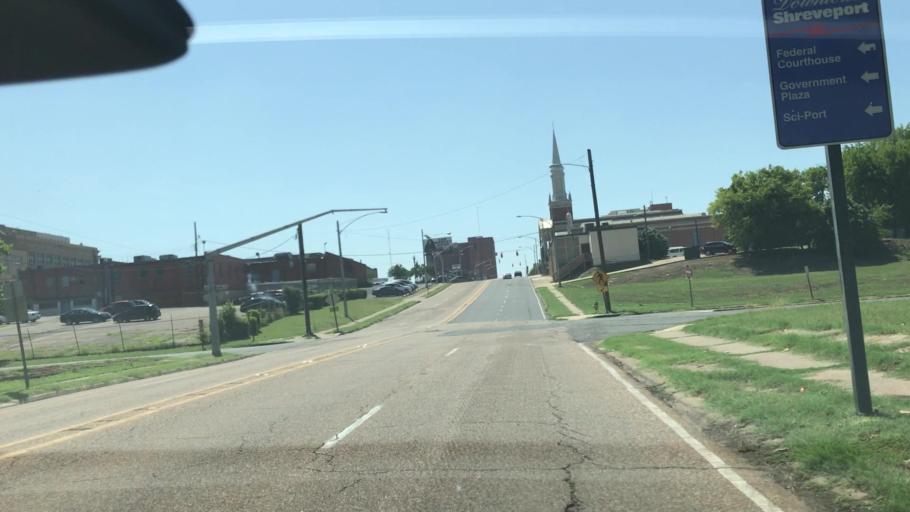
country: US
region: Louisiana
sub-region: Caddo Parish
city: Shreveport
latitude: 32.5128
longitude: -93.7547
